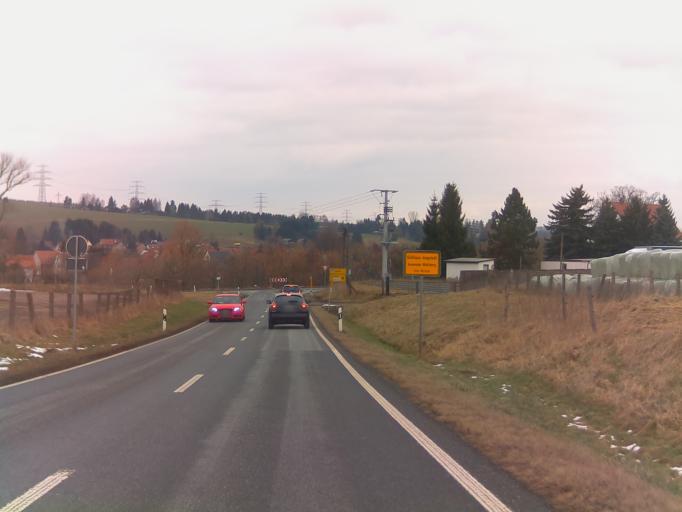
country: DE
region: Thuringia
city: Pennewitz
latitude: 50.6941
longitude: 11.0176
